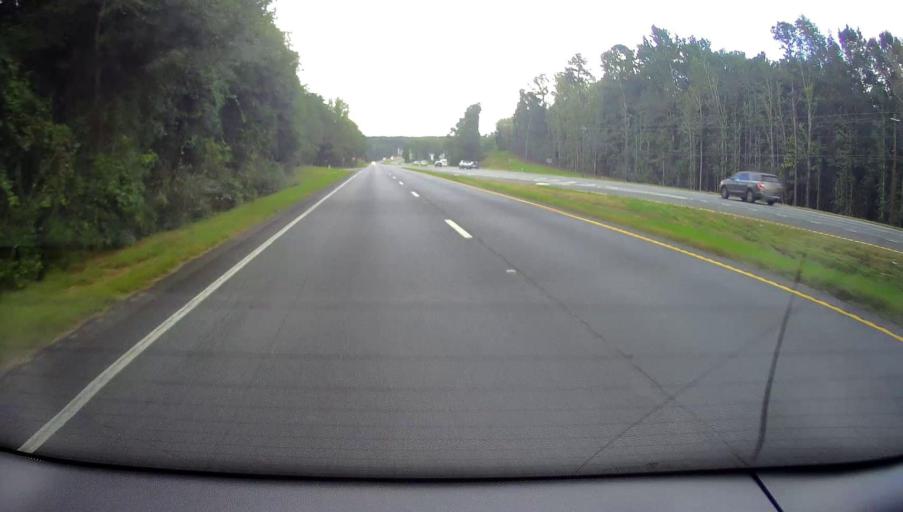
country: US
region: Georgia
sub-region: Bibb County
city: Macon
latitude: 32.9110
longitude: -83.5910
